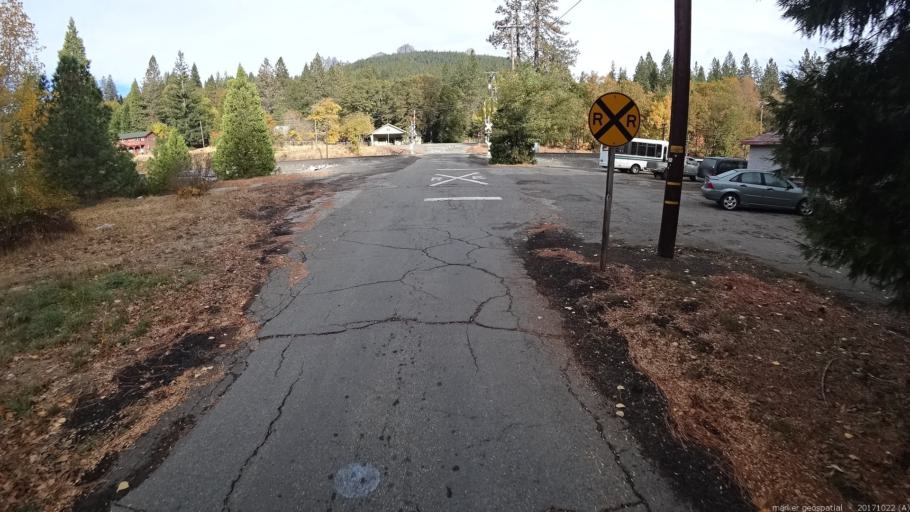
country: US
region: California
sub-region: Siskiyou County
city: Dunsmuir
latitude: 41.1491
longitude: -122.3115
